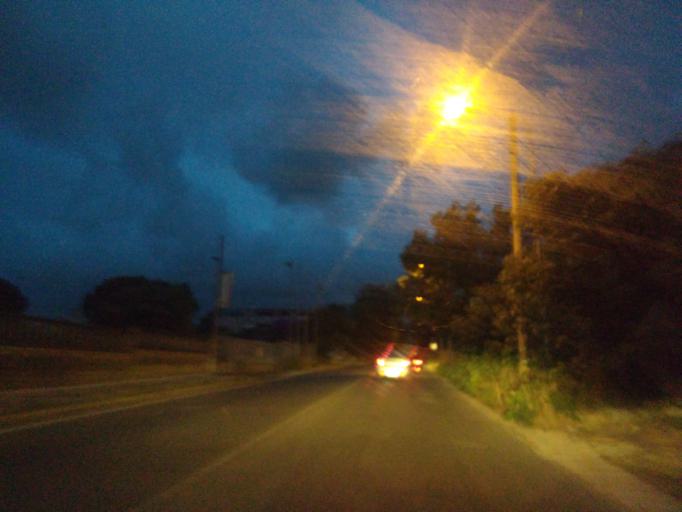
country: IT
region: Latium
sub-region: Citta metropolitana di Roma Capitale
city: Anzio
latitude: 41.4570
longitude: 12.6210
